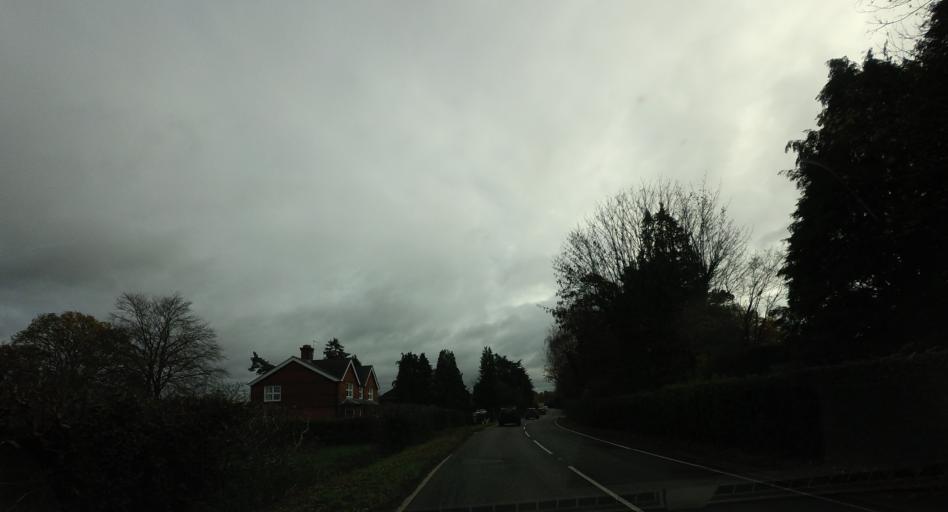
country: GB
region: England
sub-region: East Sussex
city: Northiam
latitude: 51.0233
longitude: 0.5803
